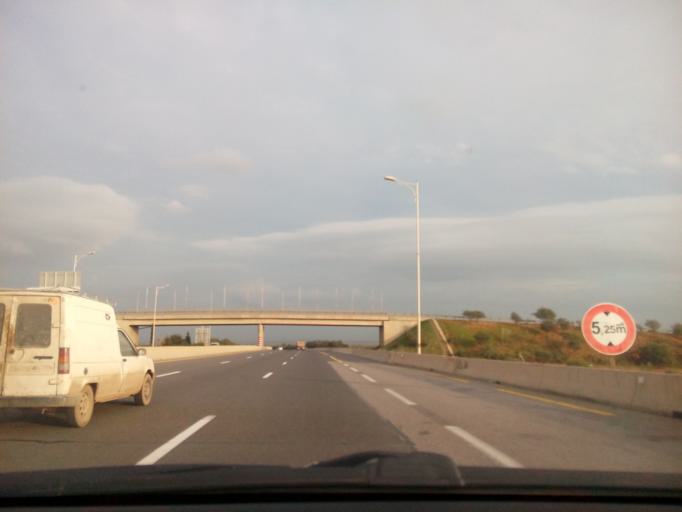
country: DZ
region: Relizane
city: Relizane
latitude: 35.7891
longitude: 0.4095
